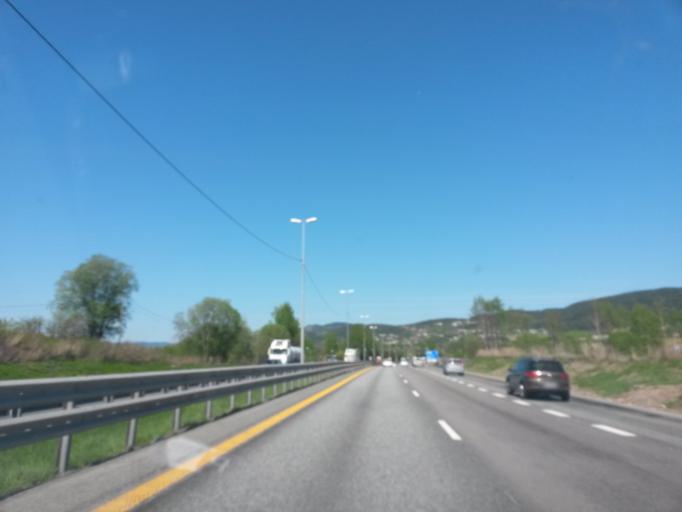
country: NO
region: Buskerud
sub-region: Lier
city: Lierbyen
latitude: 59.7627
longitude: 10.2532
